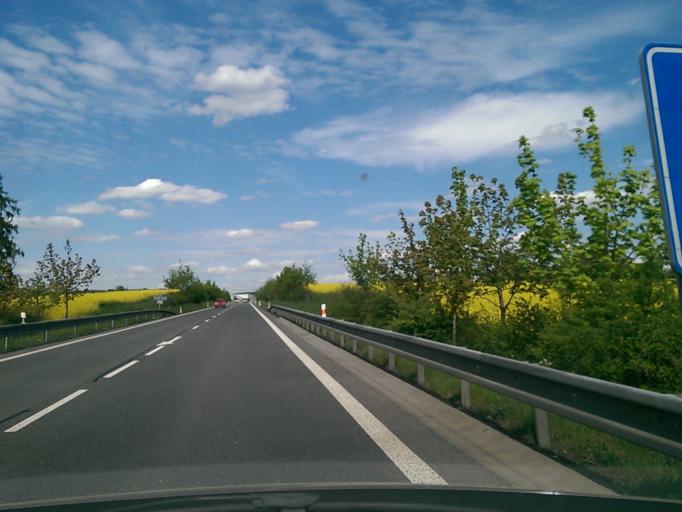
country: CZ
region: Liberecky
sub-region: Okres Semily
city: Turnov
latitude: 50.5958
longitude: 15.1434
